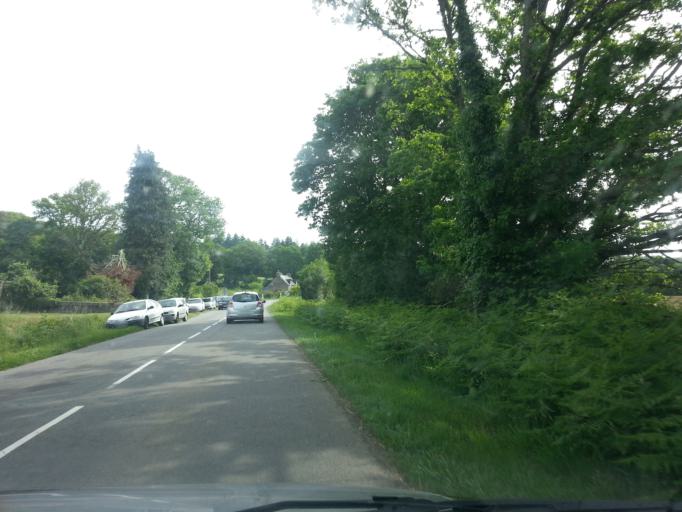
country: FR
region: Brittany
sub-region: Departement du Finistere
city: Querrien
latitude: 47.9874
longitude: -3.4934
